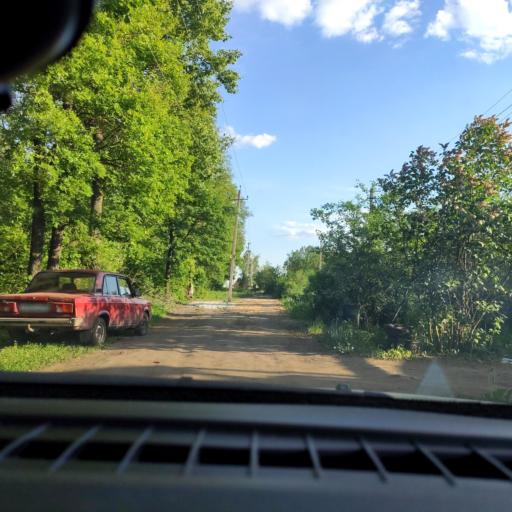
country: RU
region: Voronezj
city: Maslovka
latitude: 51.5211
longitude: 39.2387
